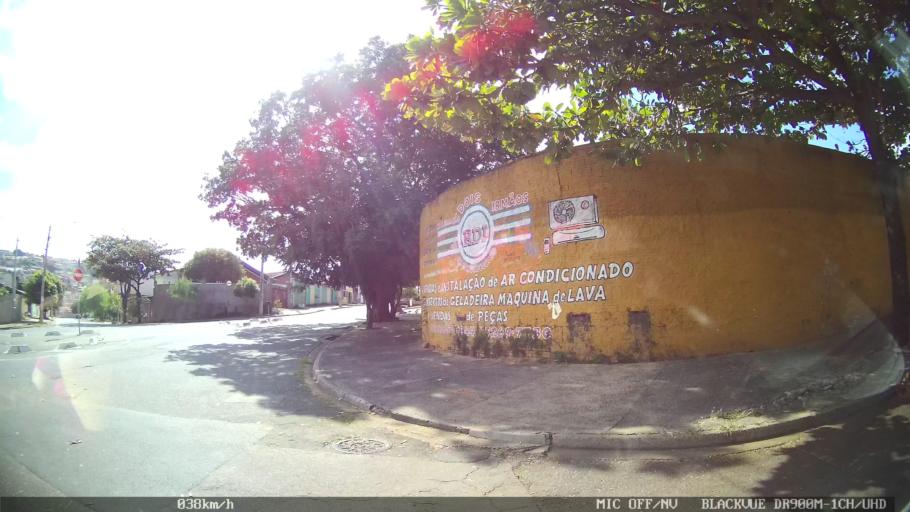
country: BR
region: Sao Paulo
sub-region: Campinas
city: Campinas
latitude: -22.9381
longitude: -47.1084
